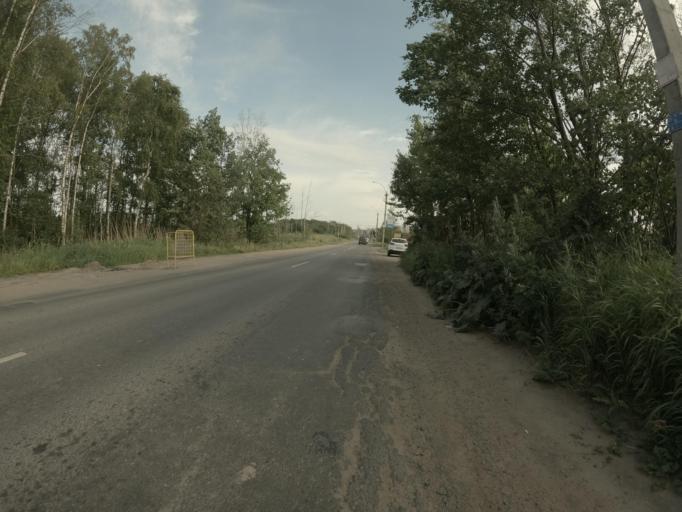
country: RU
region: St.-Petersburg
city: Krasnogvargeisky
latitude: 59.9338
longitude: 30.5204
